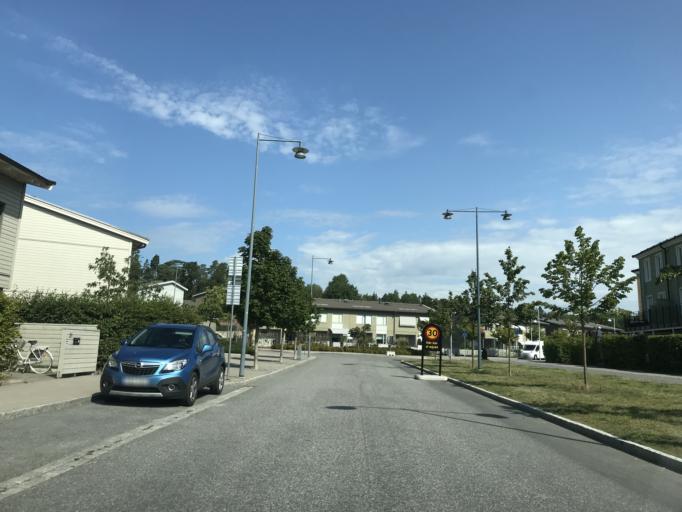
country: SE
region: Stockholm
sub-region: Solna Kommun
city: Rasunda
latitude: 59.3843
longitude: 17.9798
